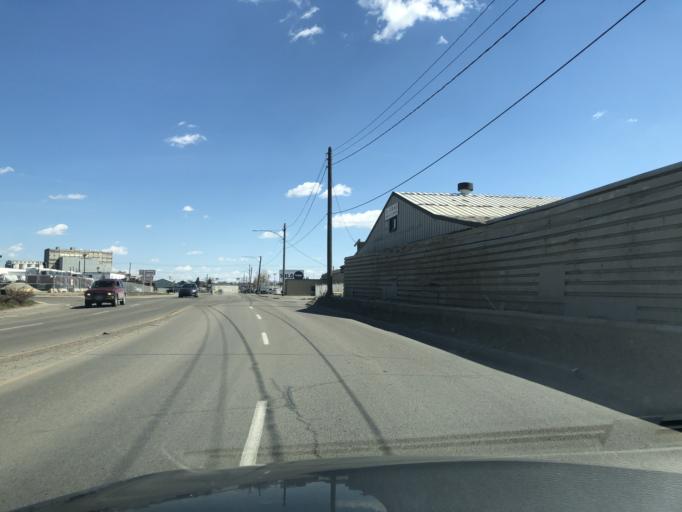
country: CA
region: Alberta
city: Calgary
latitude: 51.0186
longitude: -114.0289
